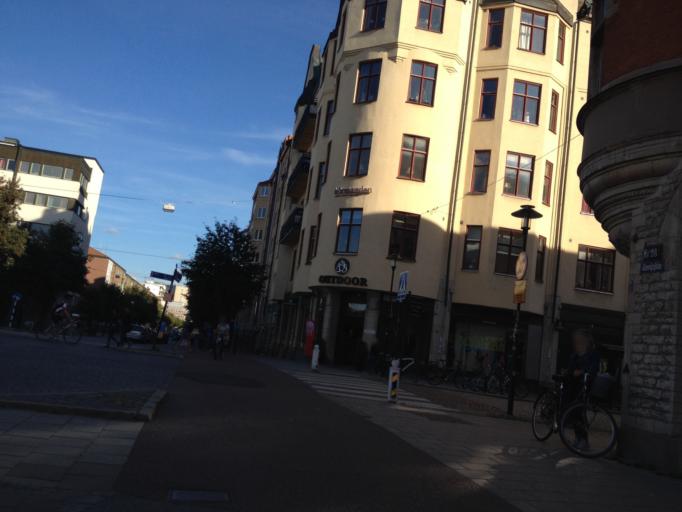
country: SE
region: OErebro
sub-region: Orebro Kommun
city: Orebro
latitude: 59.2778
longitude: 15.2158
